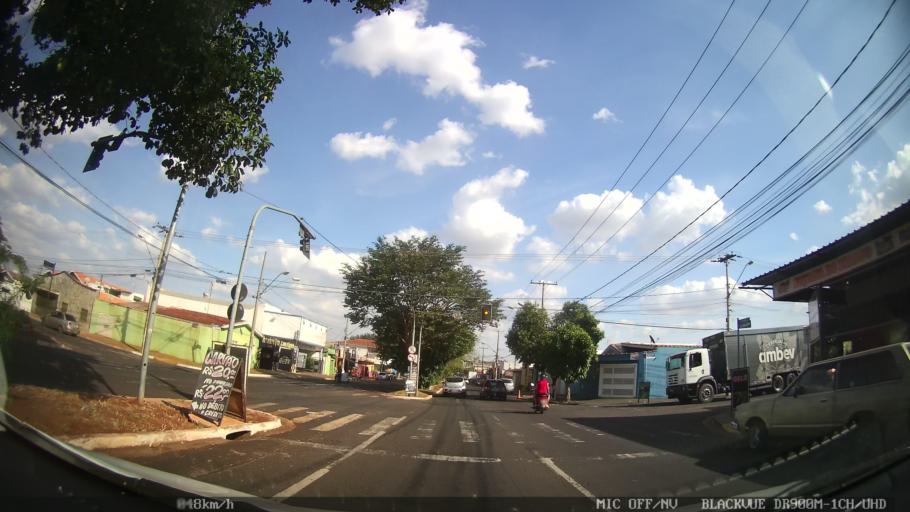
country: BR
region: Sao Paulo
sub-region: Ribeirao Preto
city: Ribeirao Preto
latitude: -21.1913
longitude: -47.8373
